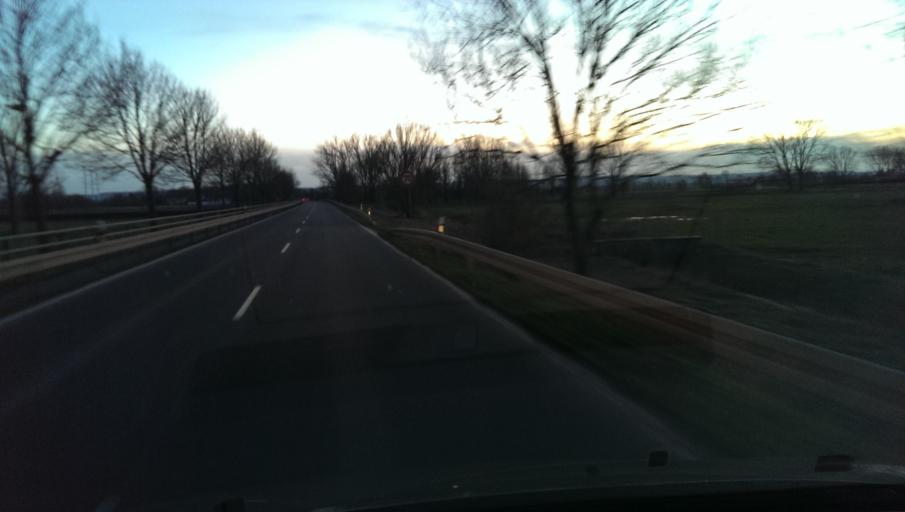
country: DE
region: Saxony-Anhalt
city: Ausleben
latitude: 52.0360
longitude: 11.0950
